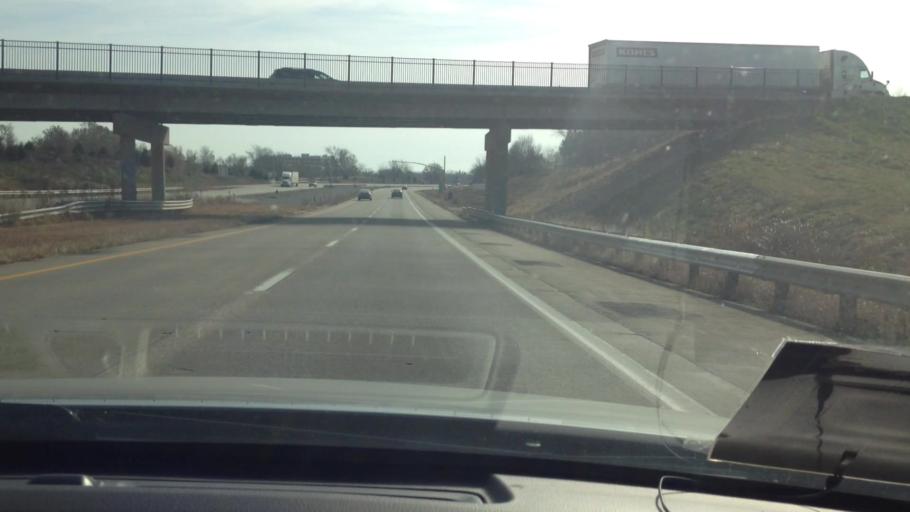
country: US
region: Missouri
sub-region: Cass County
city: Harrisonville
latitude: 38.6372
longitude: -94.3546
